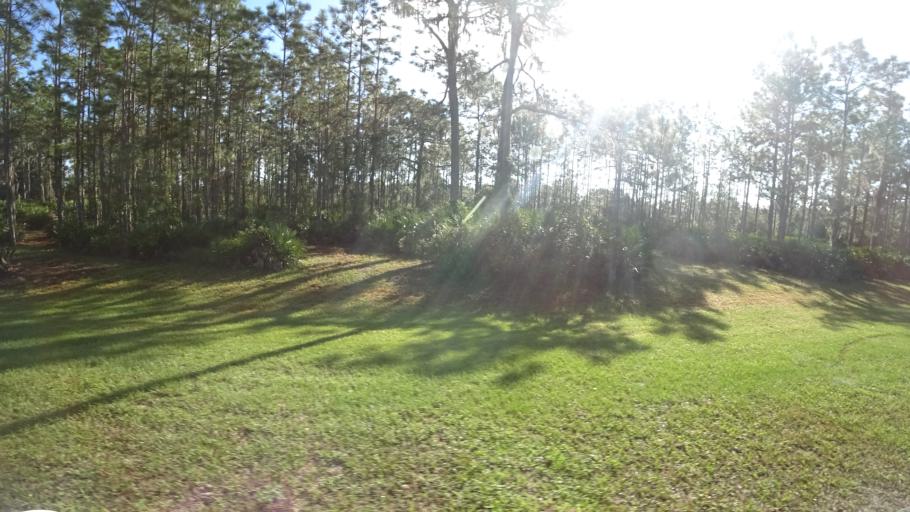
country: US
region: Florida
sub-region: Sarasota County
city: The Meadows
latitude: 27.4195
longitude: -82.3326
